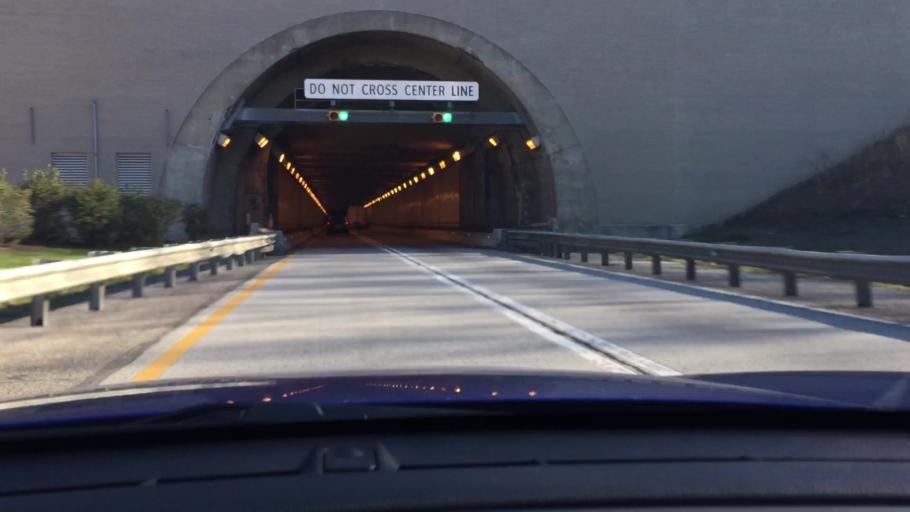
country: US
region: Pennsylvania
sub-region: Franklin County
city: Doylestown
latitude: 40.1563
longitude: -77.6773
